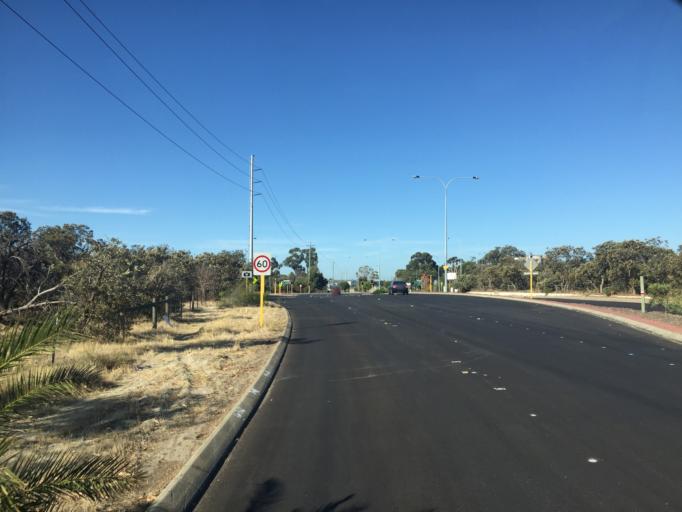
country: AU
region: Western Australia
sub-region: Canning
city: East Cannington
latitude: -31.9994
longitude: 115.9624
